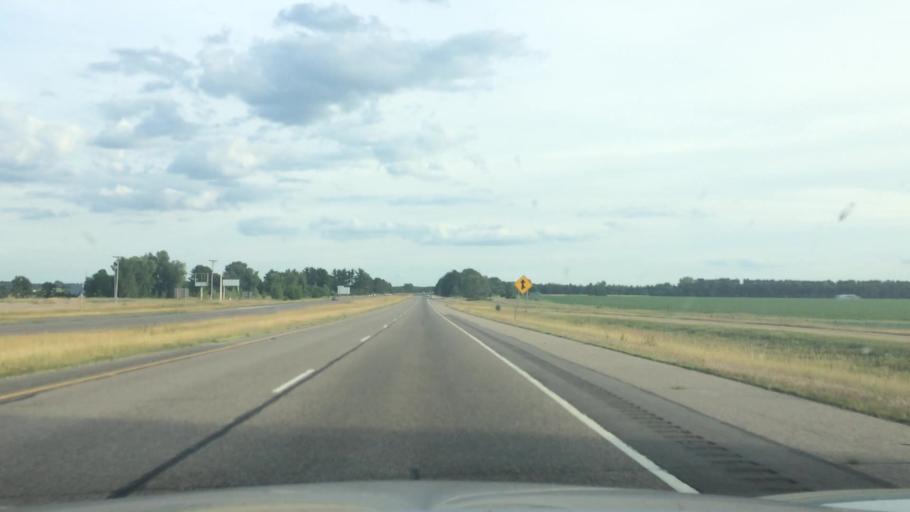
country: US
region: Wisconsin
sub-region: Portage County
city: Plover
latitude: 44.2125
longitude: -89.5247
